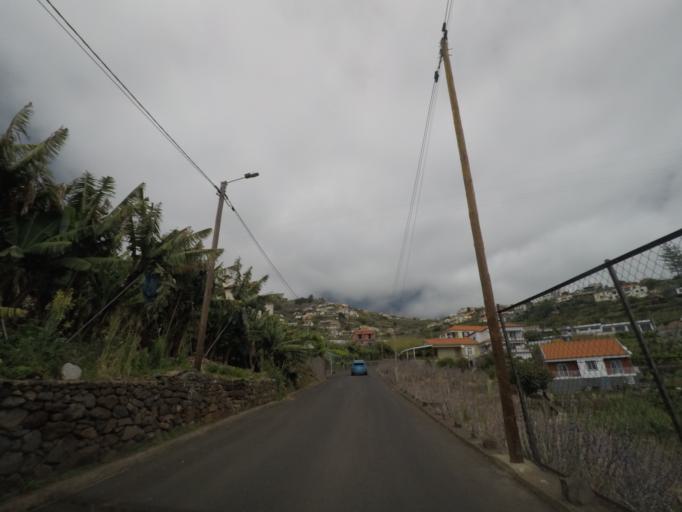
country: PT
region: Madeira
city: Ponta do Sol
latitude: 32.6913
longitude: -17.0995
